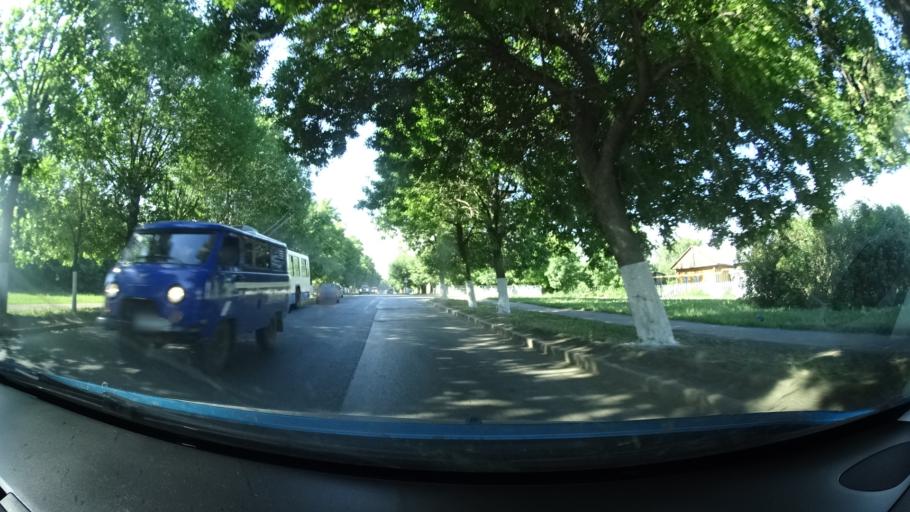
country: RU
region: Bashkortostan
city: Ufa
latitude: 54.8295
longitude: 56.0652
